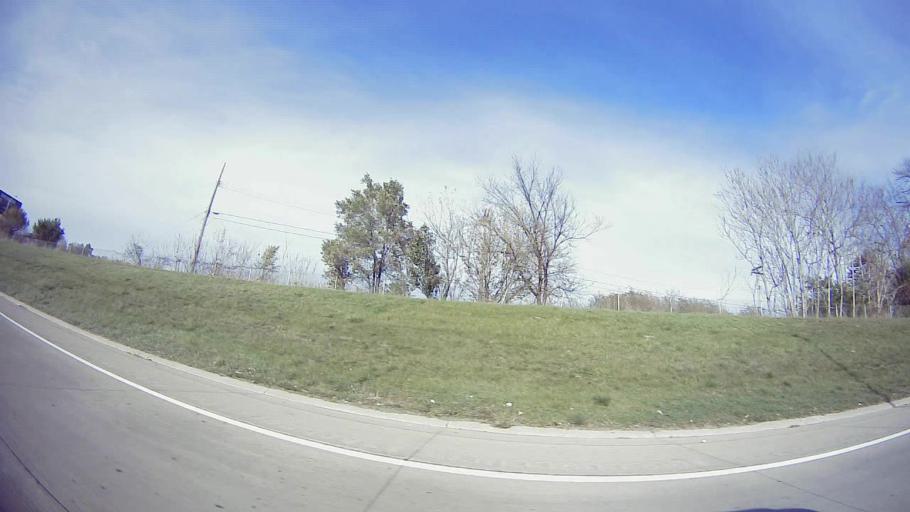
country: US
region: Michigan
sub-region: Wayne County
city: Redford
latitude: 42.3854
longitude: -83.2431
